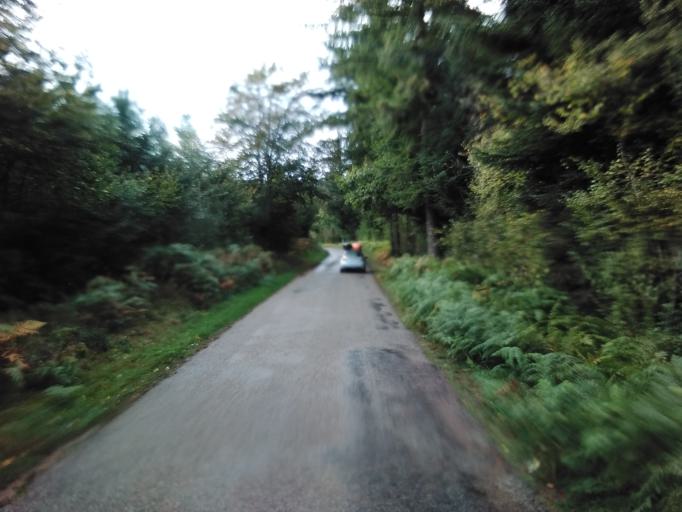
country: FR
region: Bourgogne
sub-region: Departement de la Nievre
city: Lormes
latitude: 47.2980
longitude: 3.8754
